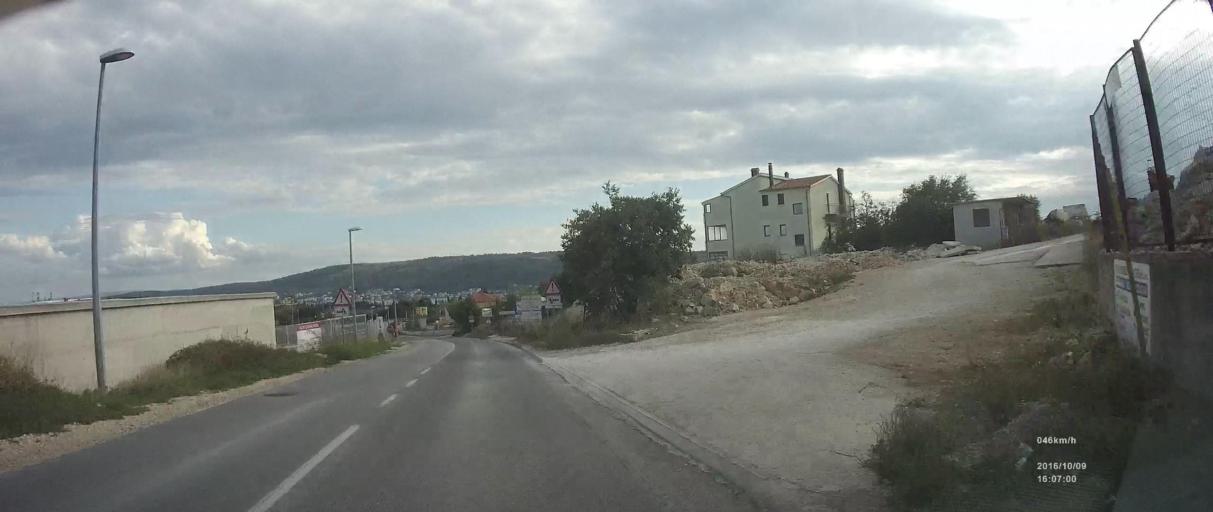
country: HR
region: Splitsko-Dalmatinska
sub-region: Grad Trogir
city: Trogir
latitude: 43.5383
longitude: 16.2849
